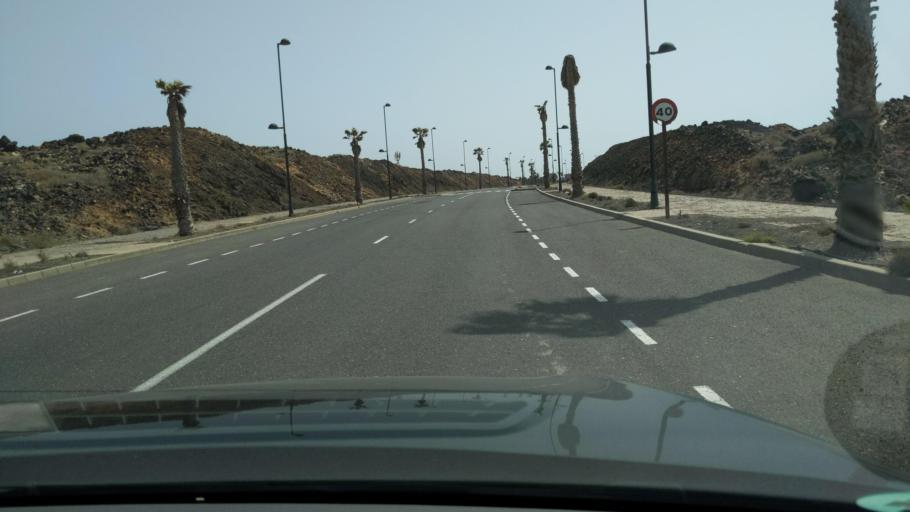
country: ES
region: Canary Islands
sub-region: Provincia de Las Palmas
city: Corralejo
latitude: 28.7367
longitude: -13.9448
